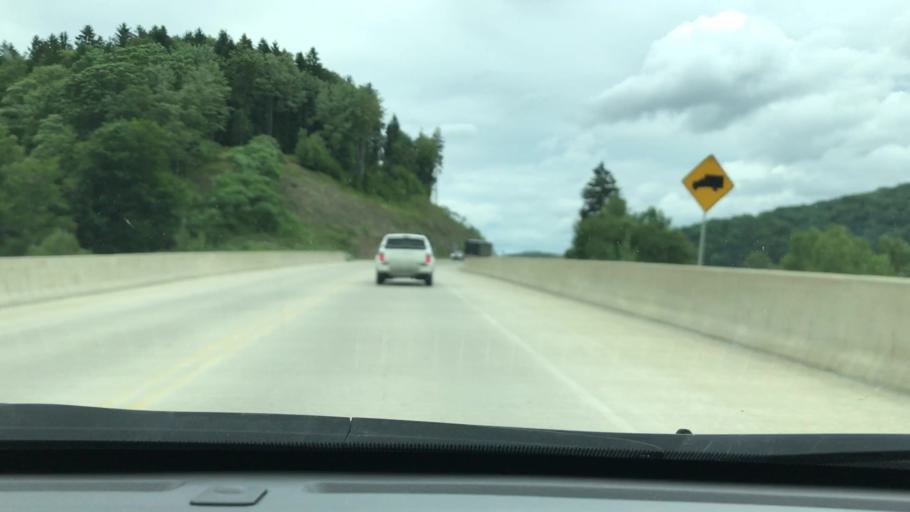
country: US
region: Pennsylvania
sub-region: Elk County
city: Johnsonburg
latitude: 41.4884
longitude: -78.6809
